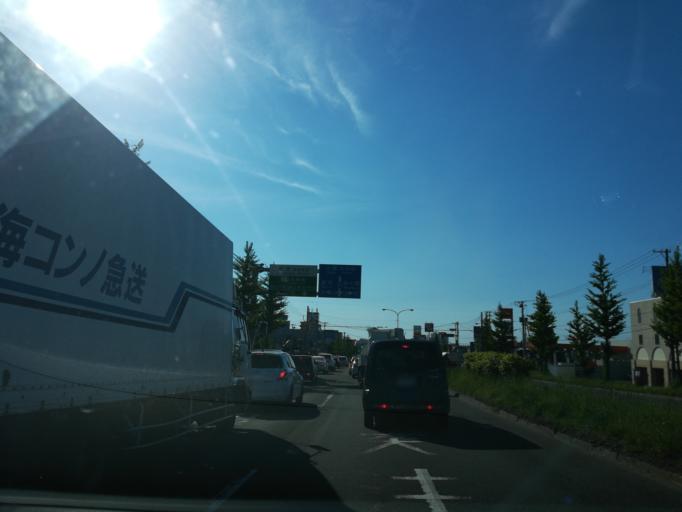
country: JP
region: Hokkaido
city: Kitahiroshima
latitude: 43.0215
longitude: 141.4729
